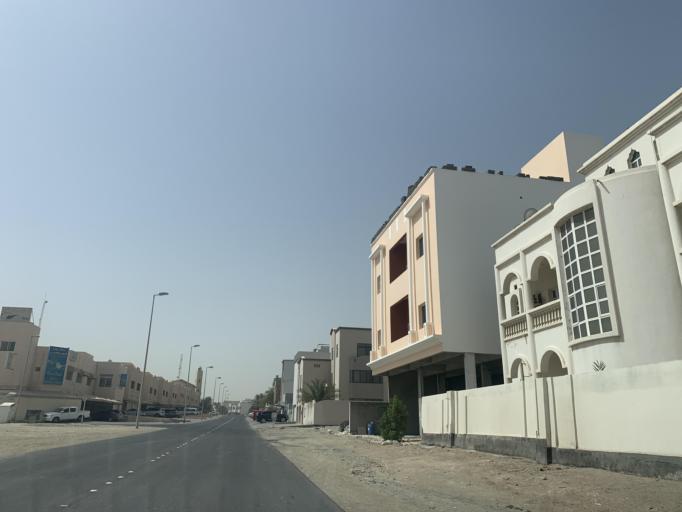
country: BH
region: Northern
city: Madinat `Isa
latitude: 26.1509
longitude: 50.5288
